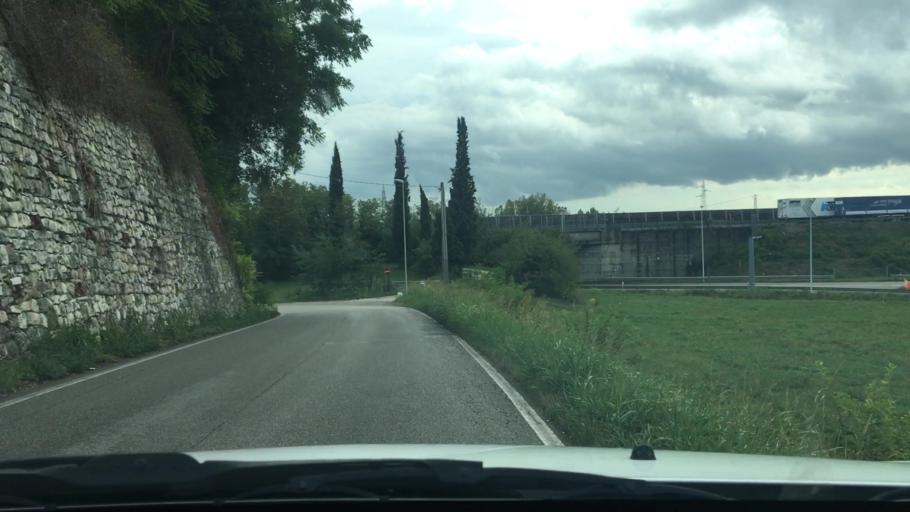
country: IT
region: Veneto
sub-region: Provincia di Verona
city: Monticelli-Fontana
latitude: 45.4214
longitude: 11.1212
